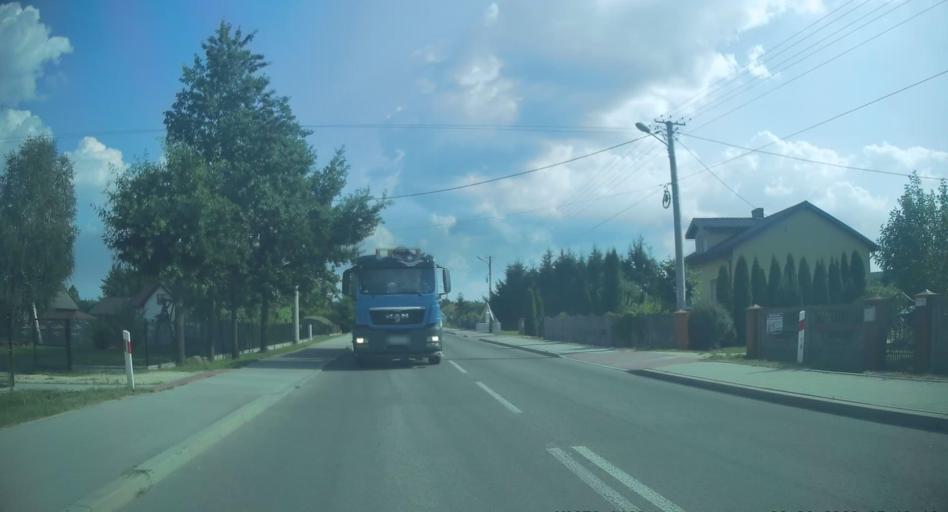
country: PL
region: Swietokrzyskie
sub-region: Powiat konecki
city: Radoszyce
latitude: 51.0484
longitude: 20.2827
